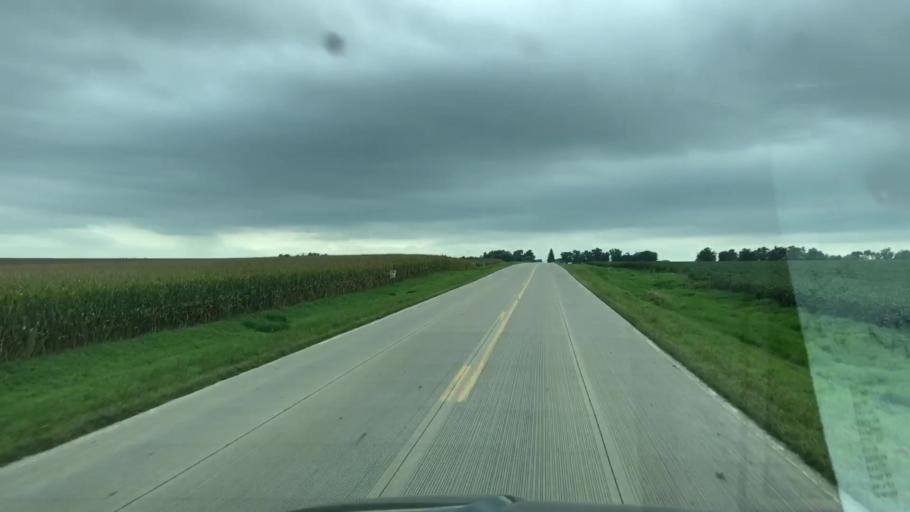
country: US
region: Iowa
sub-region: Sioux County
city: Alton
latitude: 43.1187
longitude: -95.9789
